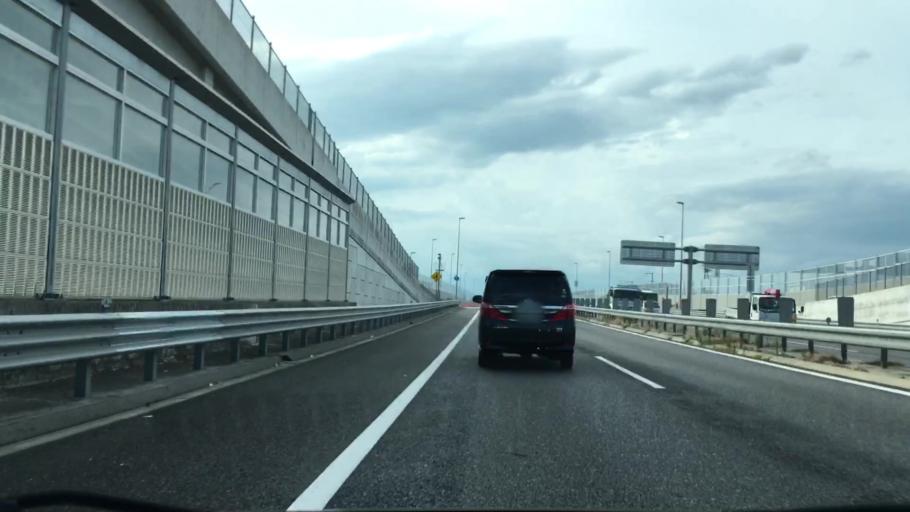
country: JP
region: Hyogo
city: Kakogawacho-honmachi
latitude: 34.7633
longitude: 134.8529
